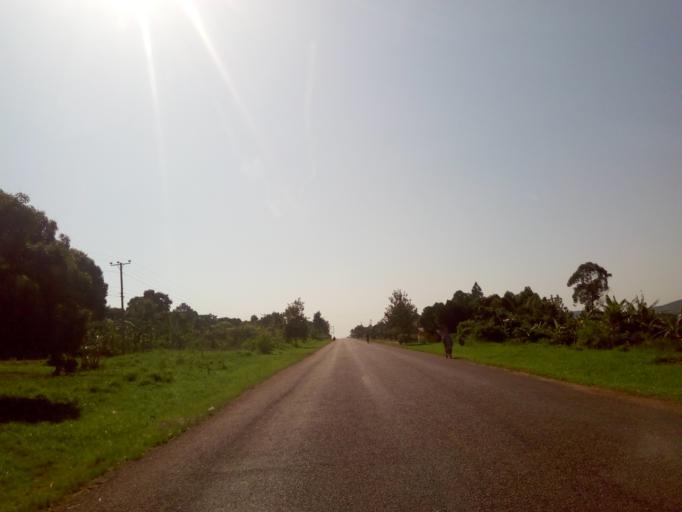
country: UG
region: Western Region
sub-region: Masindi District
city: Masindi
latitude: 1.6736
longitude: 31.7371
